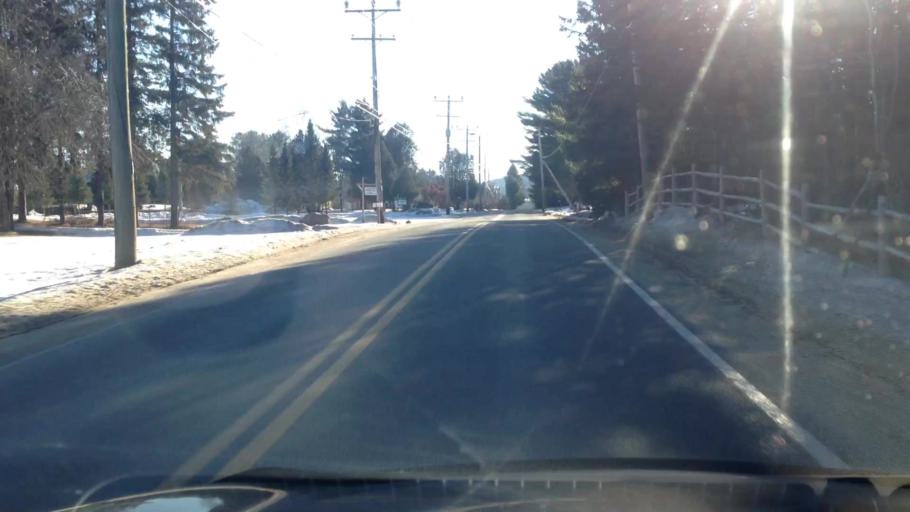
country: CA
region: Quebec
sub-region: Laurentides
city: Mont-Tremblant
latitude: 45.9801
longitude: -74.6129
